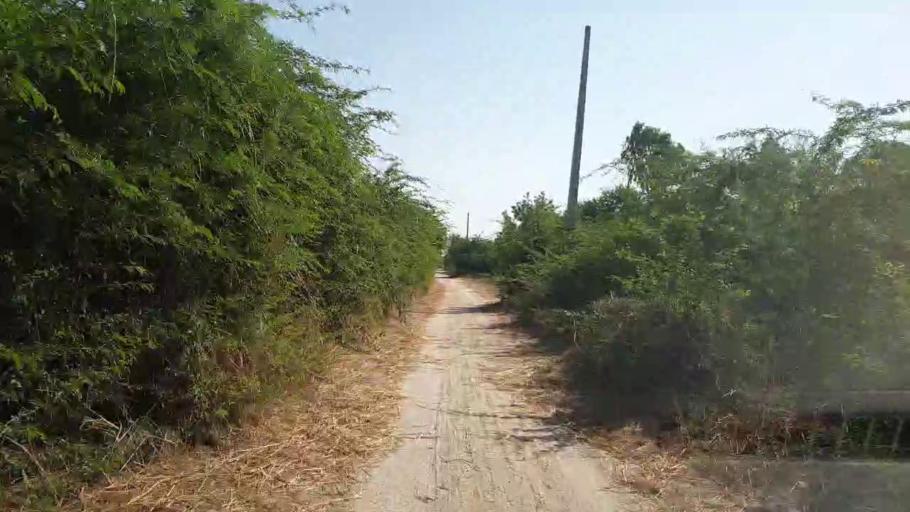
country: PK
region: Sindh
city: Tando Bago
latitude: 24.6389
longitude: 68.9905
